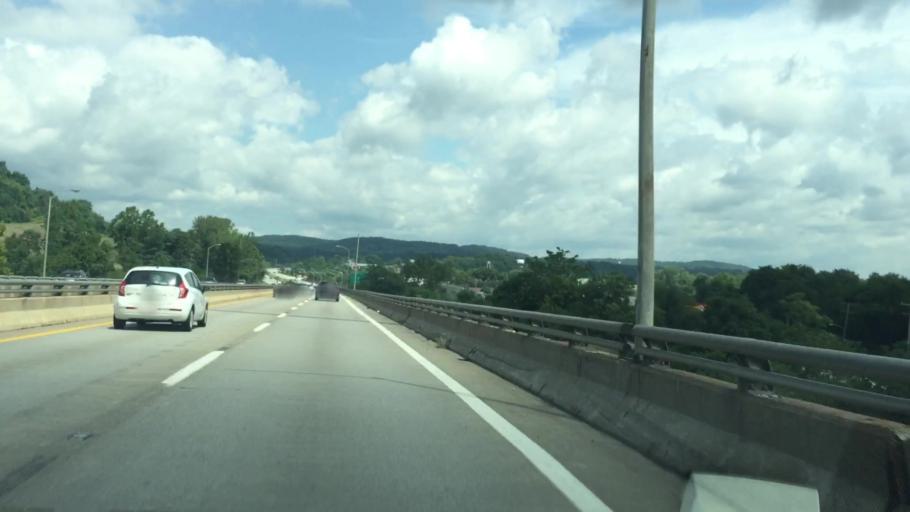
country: US
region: Pennsylvania
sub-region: Allegheny County
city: Oakmont
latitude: 40.5324
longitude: -79.8481
